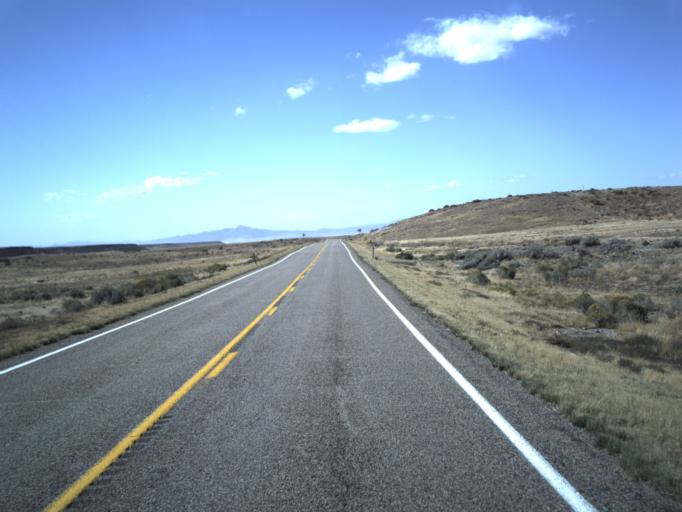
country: US
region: Utah
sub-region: Beaver County
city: Milford
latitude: 38.7771
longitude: -112.9277
